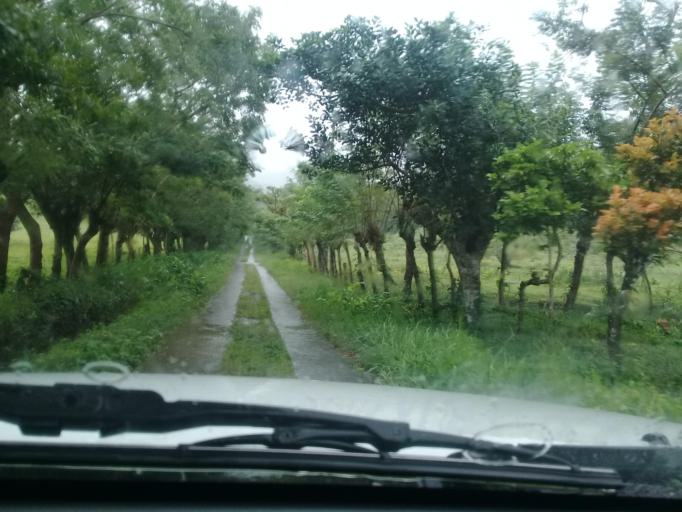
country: MX
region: Veracruz
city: Santiago Tuxtla
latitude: 18.4610
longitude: -95.3159
